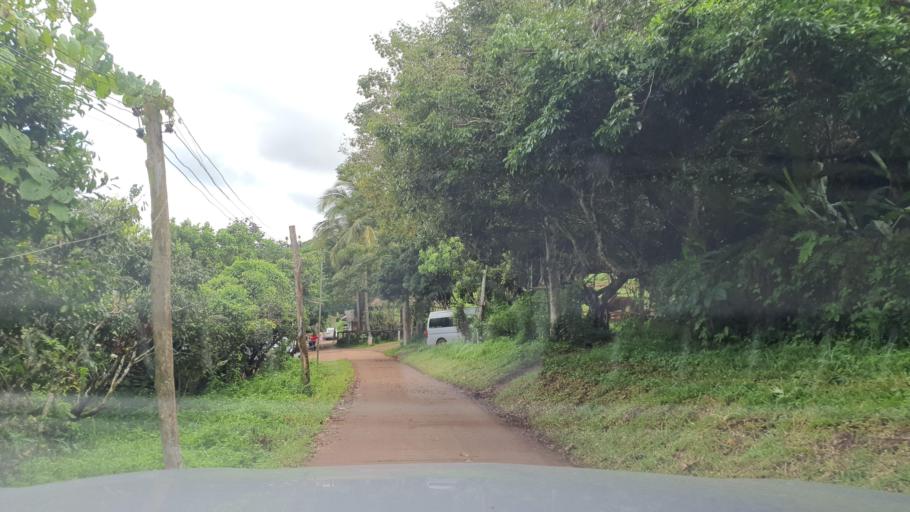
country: TH
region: Chiang Mai
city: Samoeng
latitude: 18.8045
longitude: 98.8206
